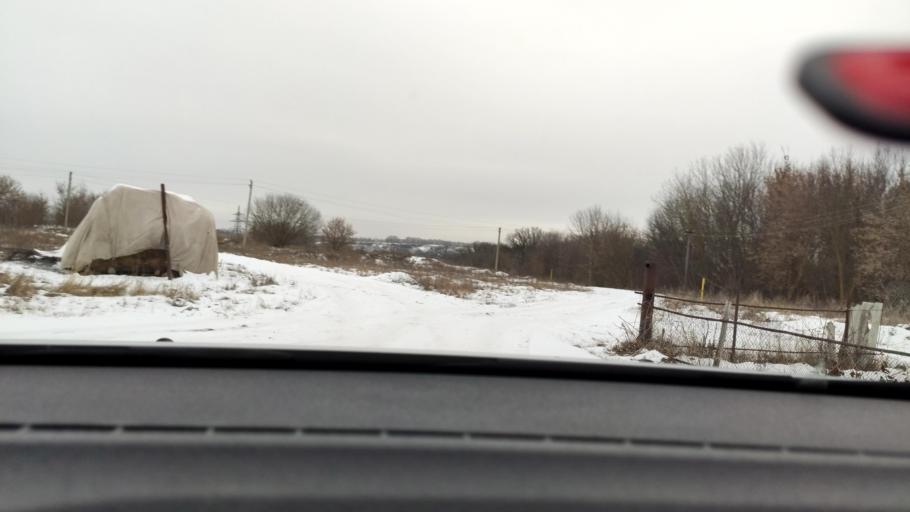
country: RU
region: Voronezj
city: Semiluki
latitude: 51.7035
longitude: 38.9775
